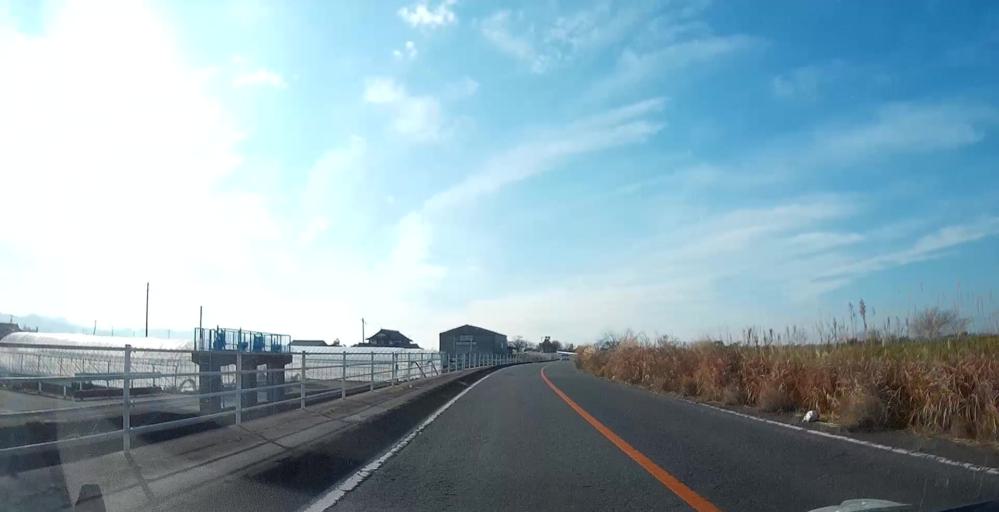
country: JP
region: Kumamoto
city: Uto
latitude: 32.7327
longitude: 130.6548
